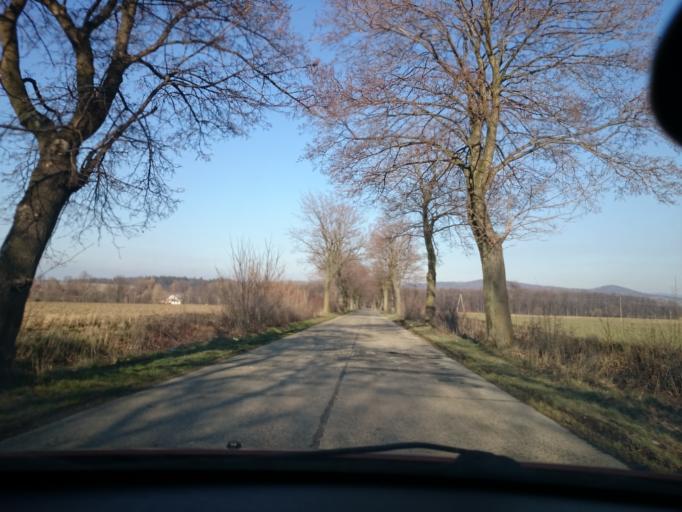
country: PL
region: Lower Silesian Voivodeship
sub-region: Powiat klodzki
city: Bystrzyca Klodzka
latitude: 50.3475
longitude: 16.5975
